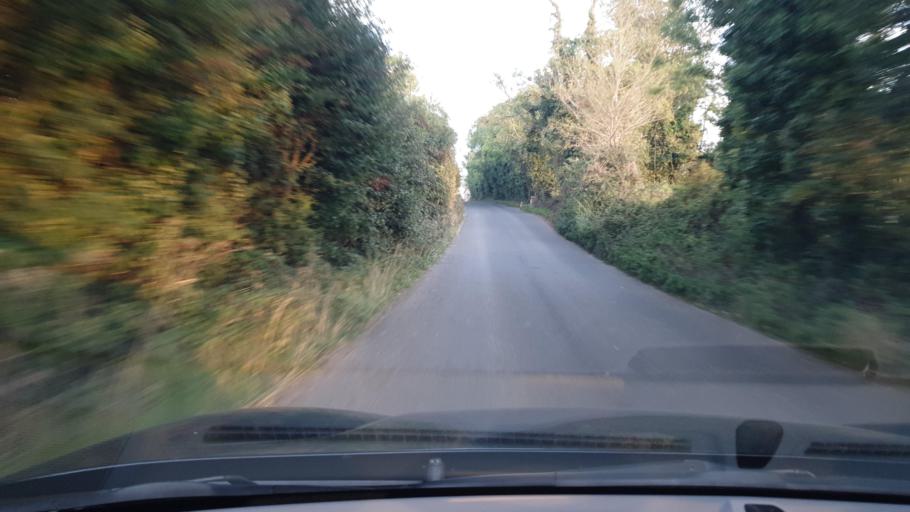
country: IE
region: Leinster
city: Balrothery
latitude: 53.5624
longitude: -6.2273
